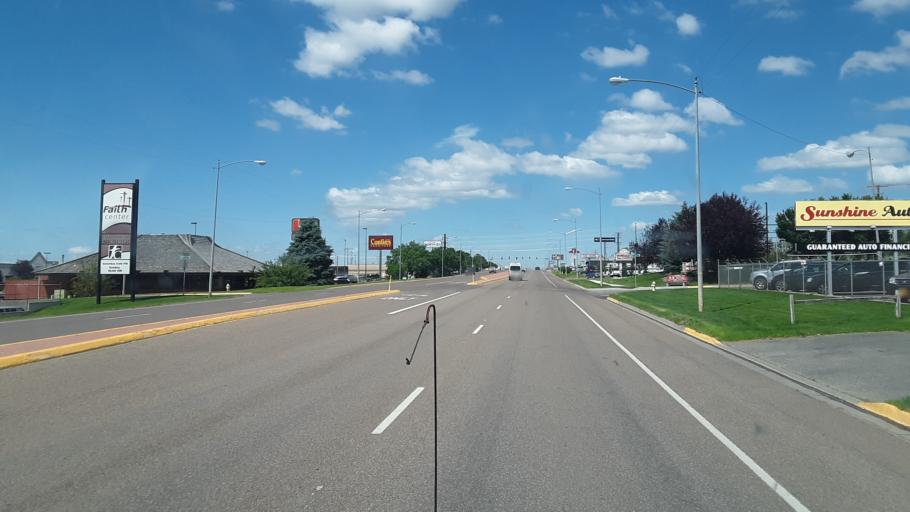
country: US
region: Montana
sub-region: Cascade County
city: Malmstrom Air Force Base
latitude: 47.4940
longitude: -111.2279
